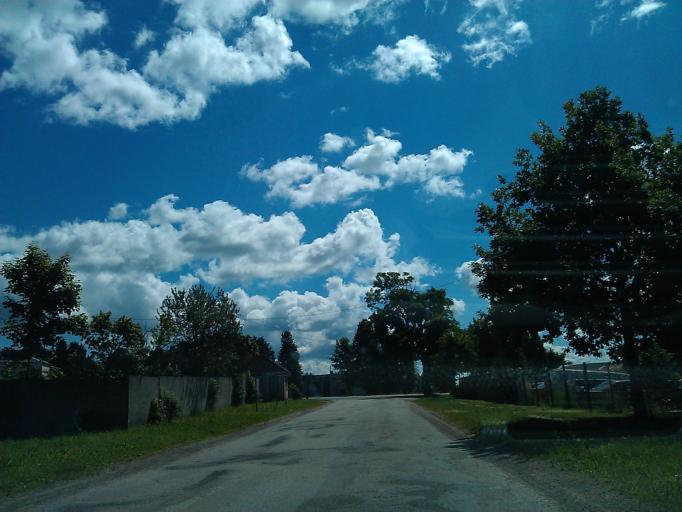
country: LV
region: Varaklani
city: Varaklani
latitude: 56.6049
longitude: 26.7728
